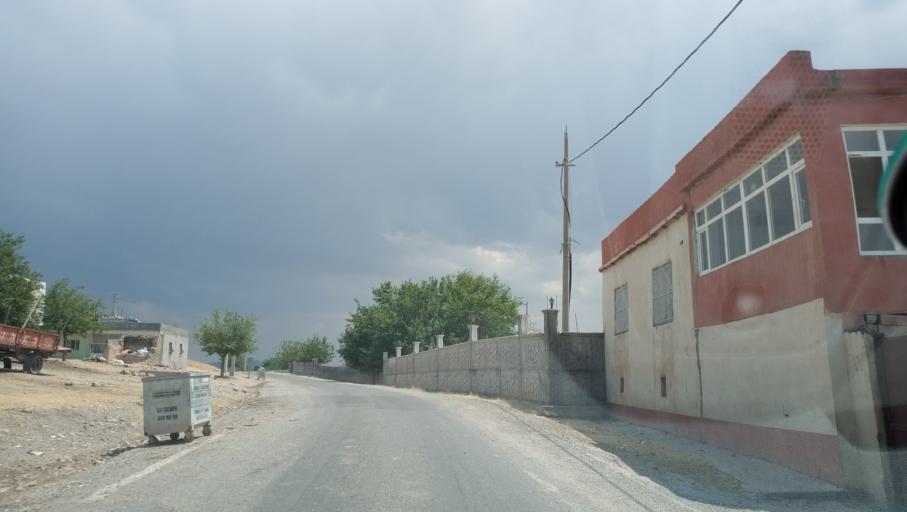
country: TR
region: Mardin
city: Baskavak
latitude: 37.6802
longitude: 40.8477
